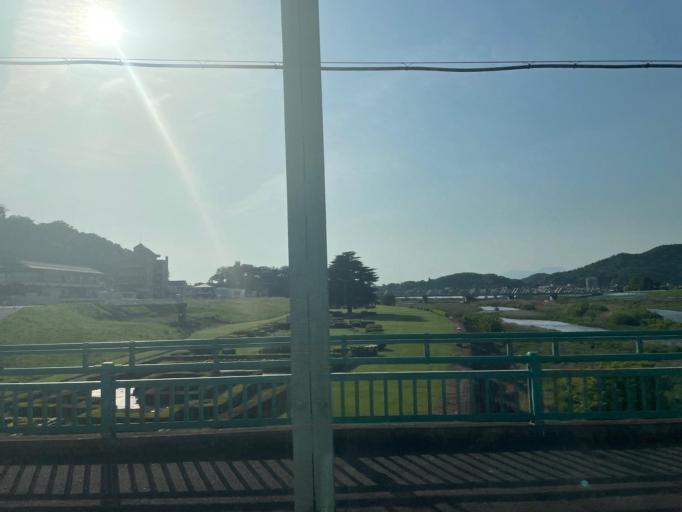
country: JP
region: Tochigi
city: Ashikaga
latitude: 36.3312
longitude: 139.4483
